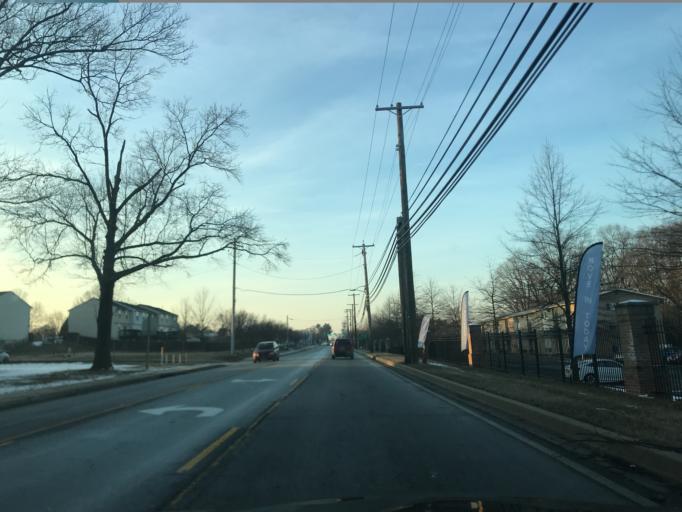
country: US
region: Maryland
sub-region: Harford County
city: Edgewood
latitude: 39.4245
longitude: -76.2964
